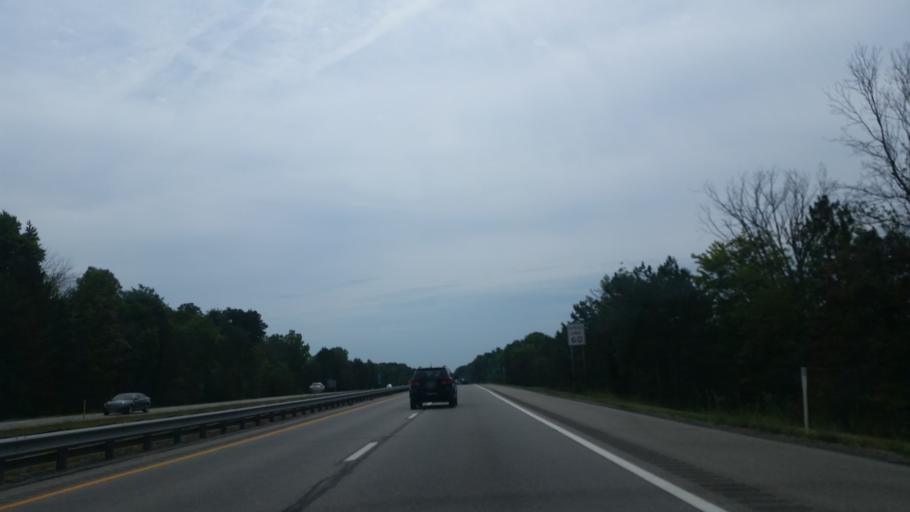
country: US
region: Ohio
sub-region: Cuyahoga County
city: Solon
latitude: 41.4004
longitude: -81.4577
